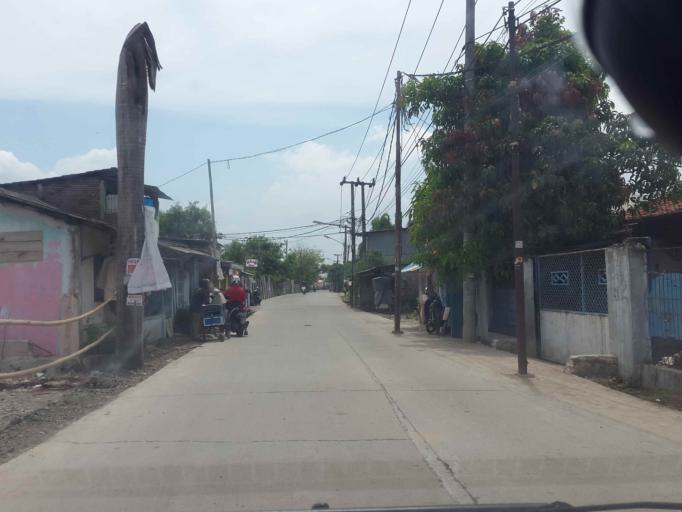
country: ID
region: West Java
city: Teluknaga
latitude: -6.1282
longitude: 106.6181
